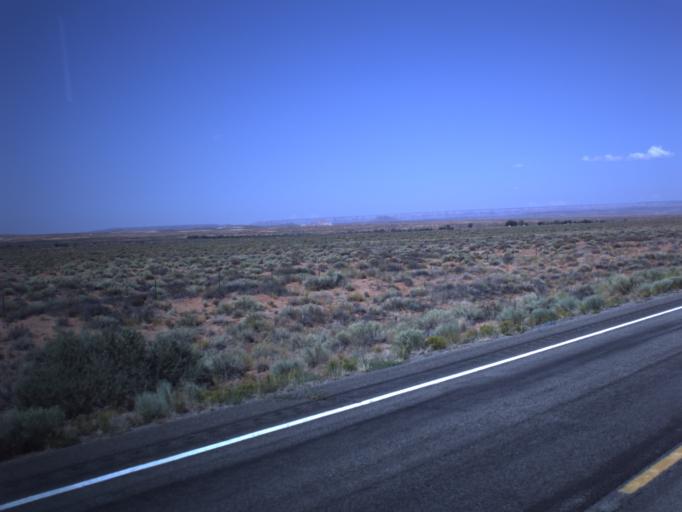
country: US
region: Utah
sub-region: San Juan County
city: Blanding
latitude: 37.1286
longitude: -109.5492
